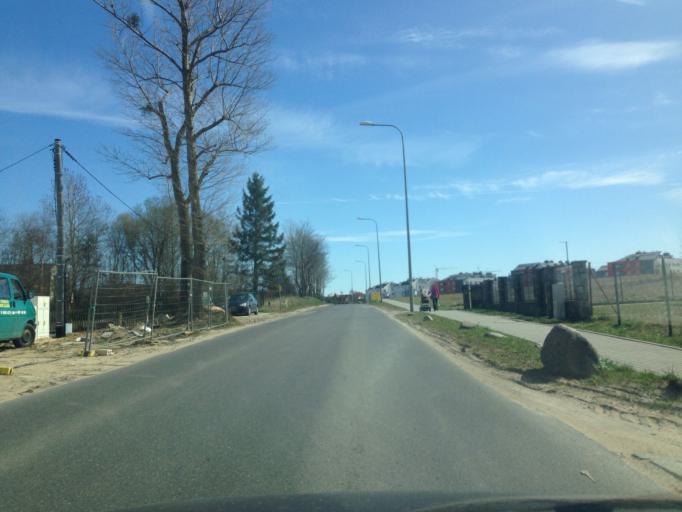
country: PL
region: Pomeranian Voivodeship
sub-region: Powiat wejherowski
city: Bojano
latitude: 54.4897
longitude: 18.4252
